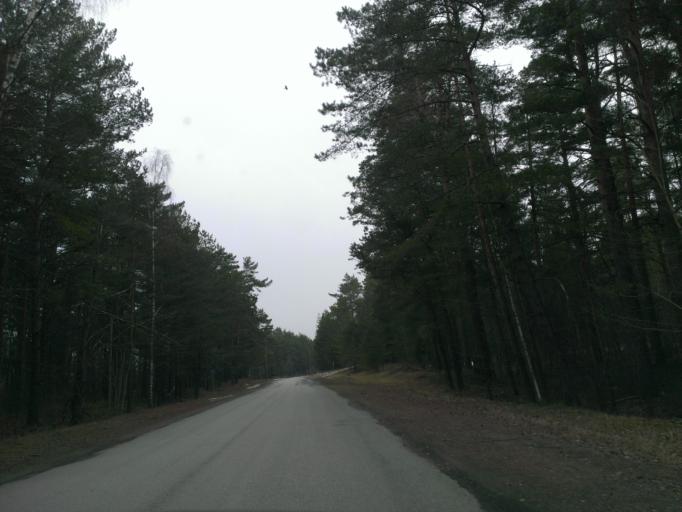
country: LV
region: Salacgrivas
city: Ainazi
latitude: 58.0206
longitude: 24.4543
